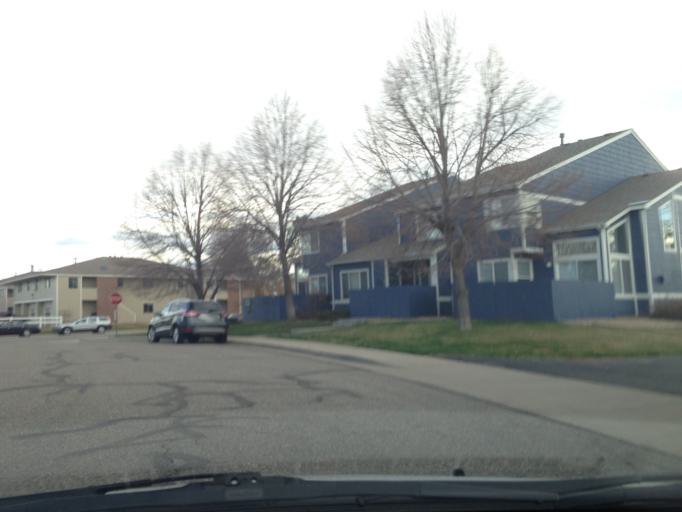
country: US
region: Colorado
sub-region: Boulder County
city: Lafayette
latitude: 39.9856
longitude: -105.1060
